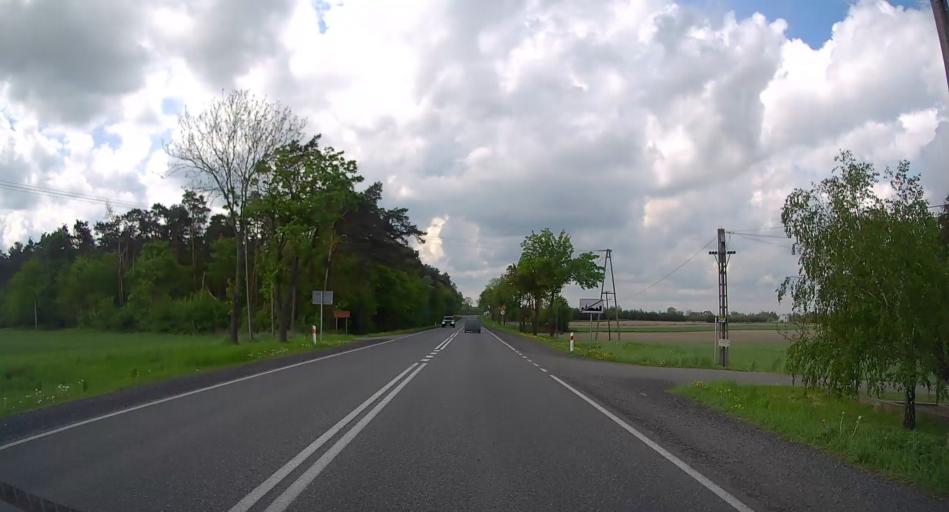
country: PL
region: Masovian Voivodeship
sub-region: Powiat nowodworski
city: Zakroczym
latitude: 52.4470
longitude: 20.5842
